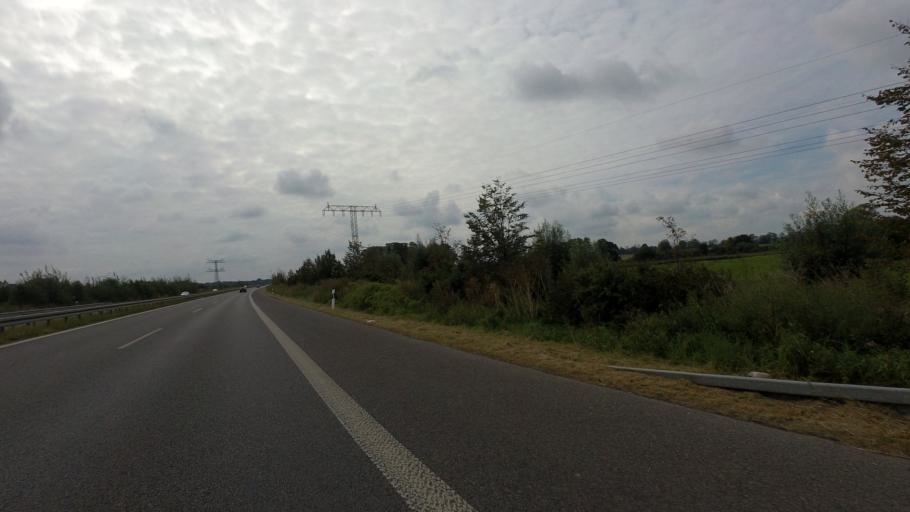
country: DE
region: Brandenburg
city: Rangsdorf
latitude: 52.3354
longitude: 13.4450
